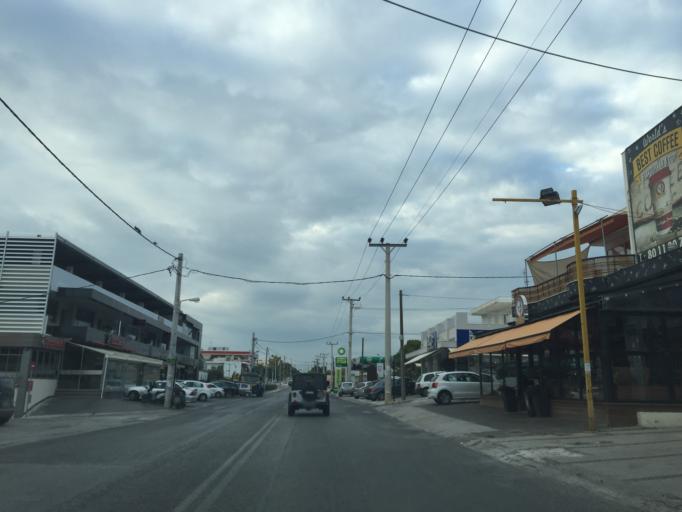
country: GR
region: Attica
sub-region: Nomarchia Anatolikis Attikis
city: Vari
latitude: 37.8337
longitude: 23.8008
